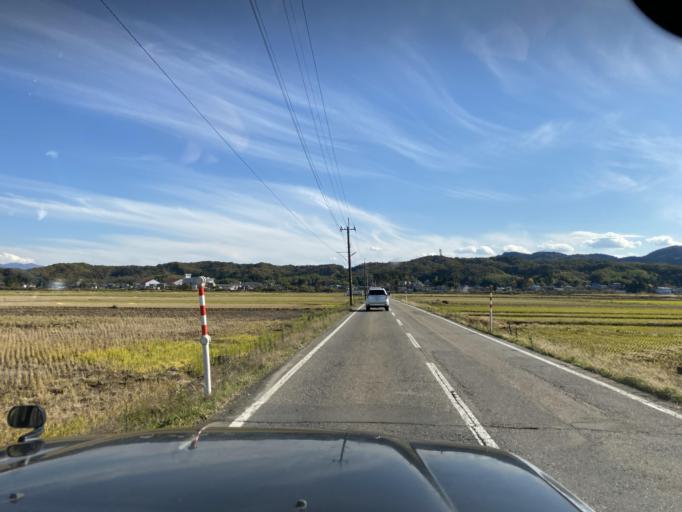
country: JP
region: Niigata
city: Niitsu-honcho
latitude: 37.7562
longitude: 139.0919
